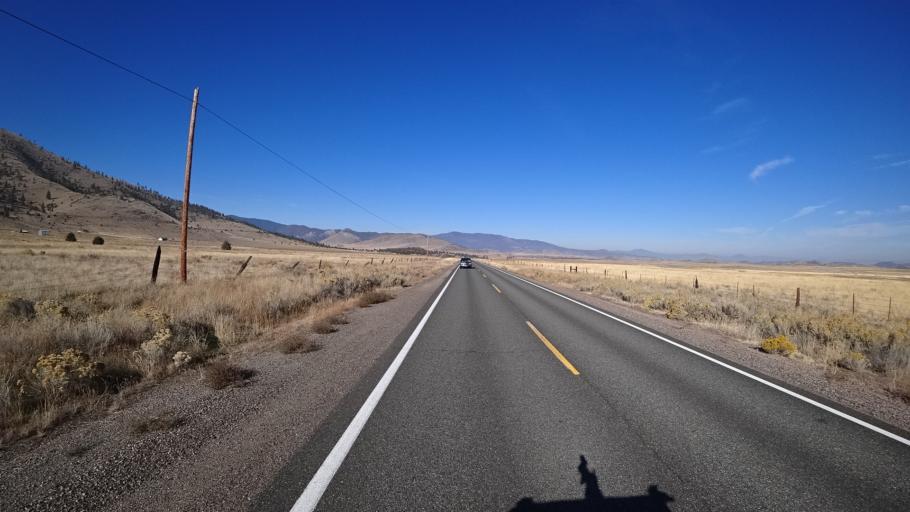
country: US
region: California
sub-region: Siskiyou County
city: Weed
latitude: 41.4811
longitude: -122.4952
